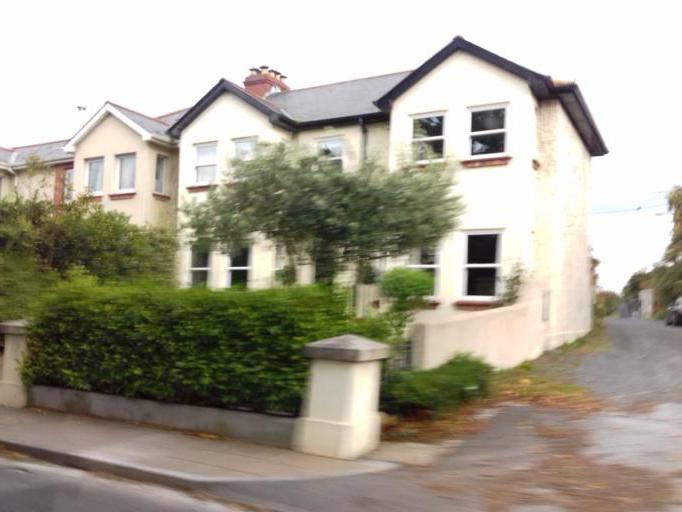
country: IE
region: Leinster
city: Dalkey
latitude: 53.2811
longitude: -6.1072
